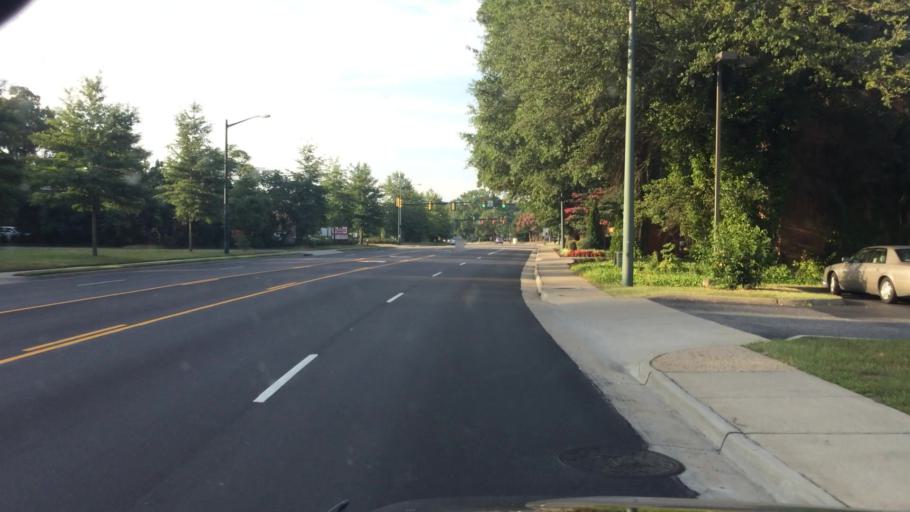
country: US
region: Virginia
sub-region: City of Williamsburg
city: Williamsburg
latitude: 37.2846
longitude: -76.7200
